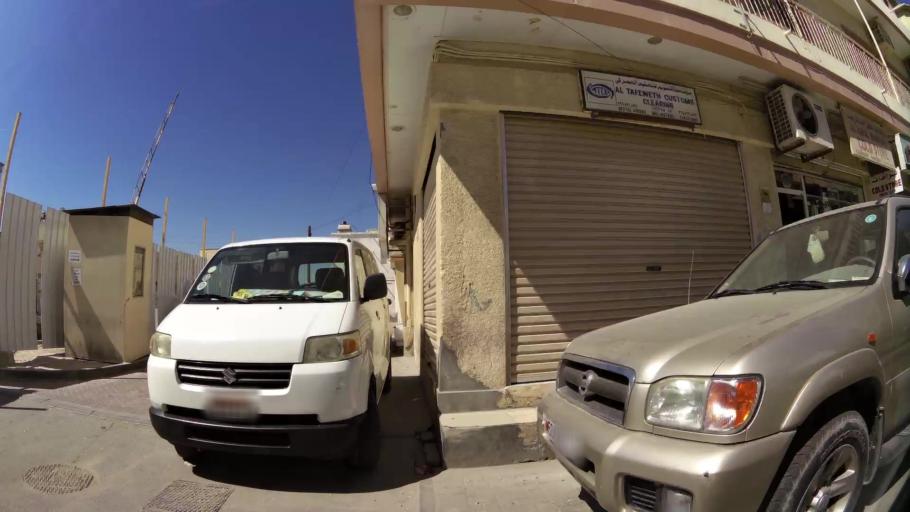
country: BH
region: Muharraq
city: Al Muharraq
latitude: 26.2539
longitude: 50.6124
